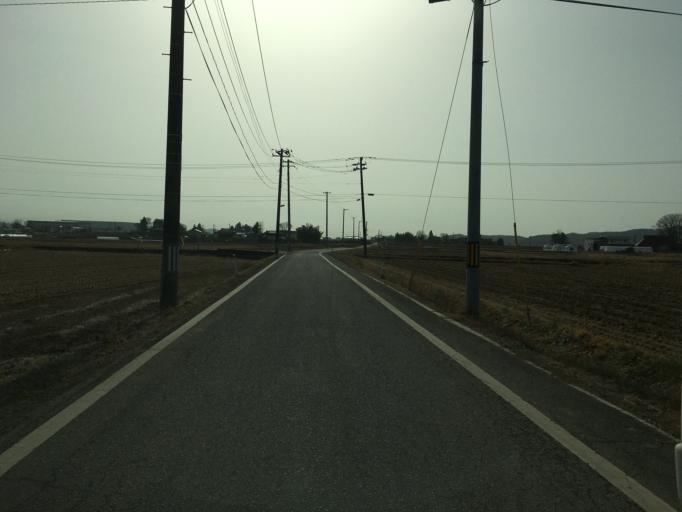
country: JP
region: Fukushima
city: Motomiya
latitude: 37.5386
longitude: 140.3913
